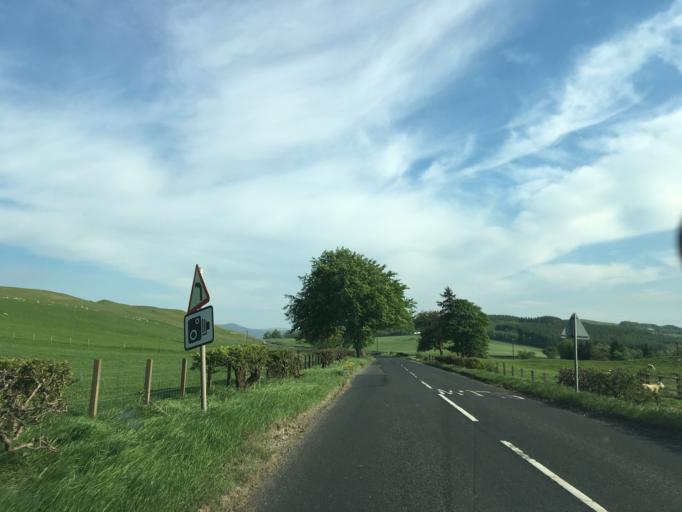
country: GB
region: Scotland
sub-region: South Lanarkshire
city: Biggar
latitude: 55.6516
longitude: -3.4336
